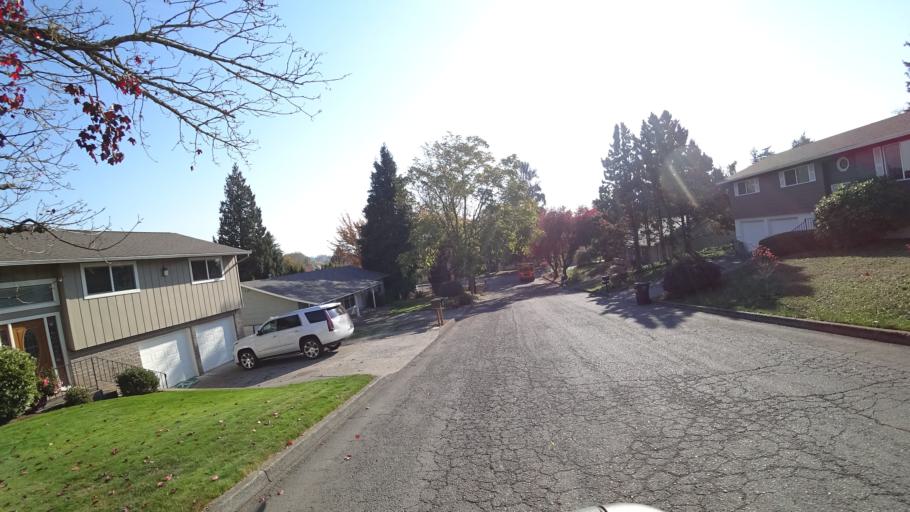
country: US
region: Oregon
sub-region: Multnomah County
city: Gresham
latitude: 45.5126
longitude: -122.4271
